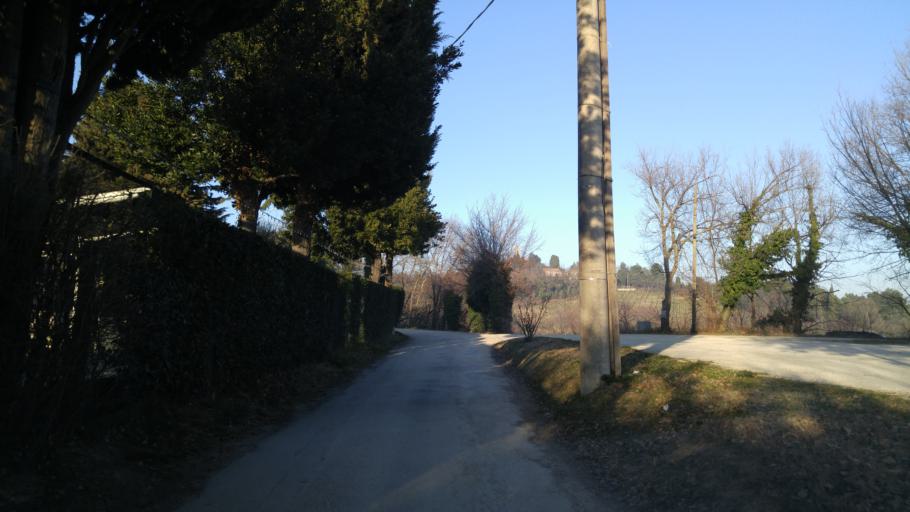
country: IT
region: The Marches
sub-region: Provincia di Pesaro e Urbino
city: Fenile
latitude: 43.8603
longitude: 12.9490
